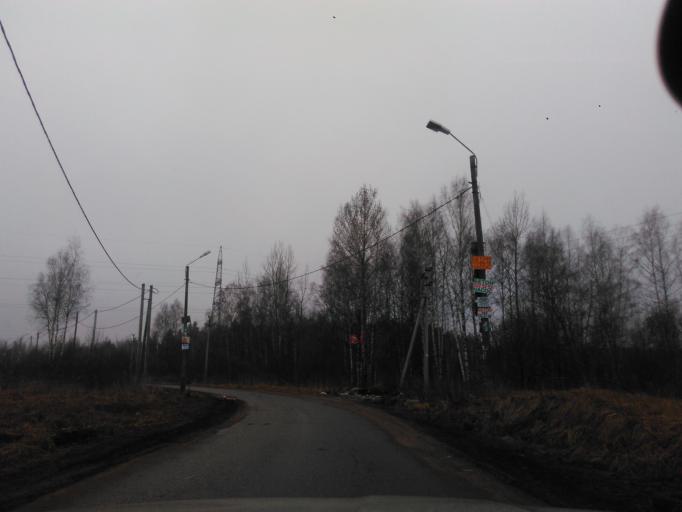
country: RU
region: Moskovskaya
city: Andreyevka
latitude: 55.9275
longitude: 37.1502
